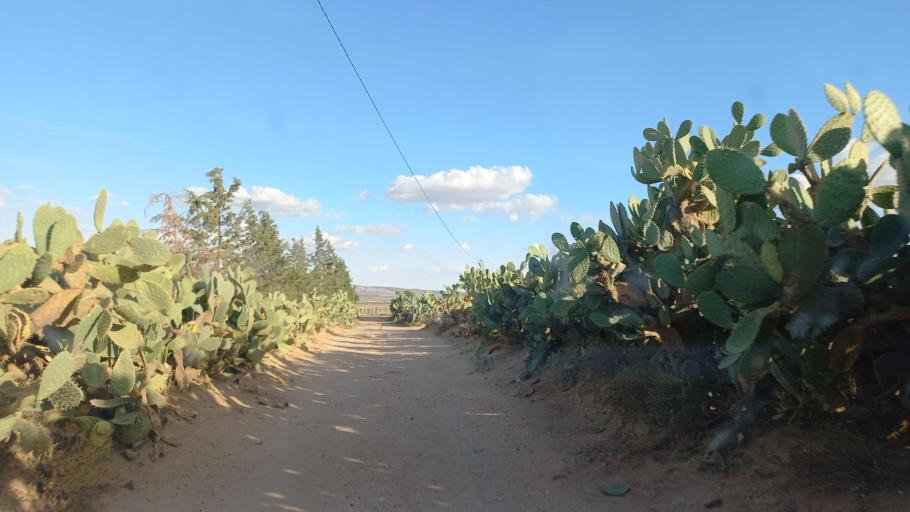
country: TN
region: Al Qasrayn
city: Sbiba
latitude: 35.3799
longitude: 9.0219
